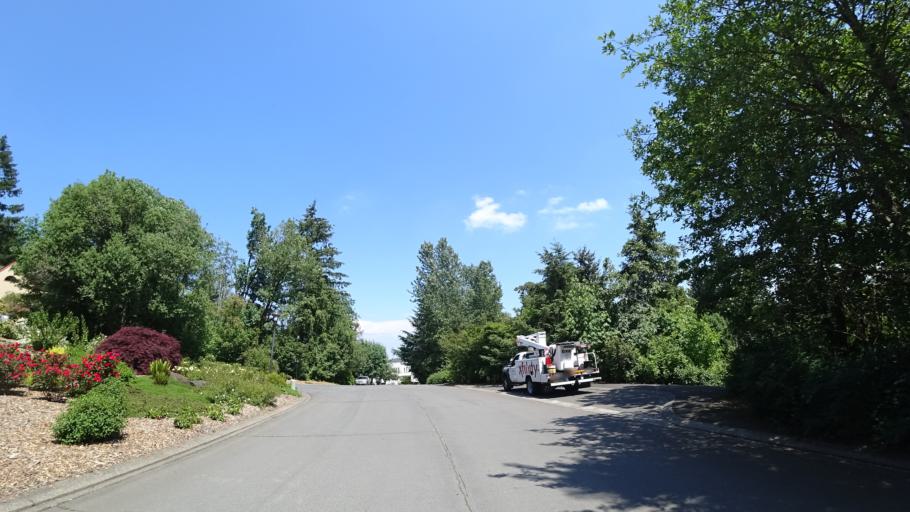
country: US
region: Oregon
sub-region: Washington County
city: Metzger
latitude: 45.4364
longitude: -122.7201
